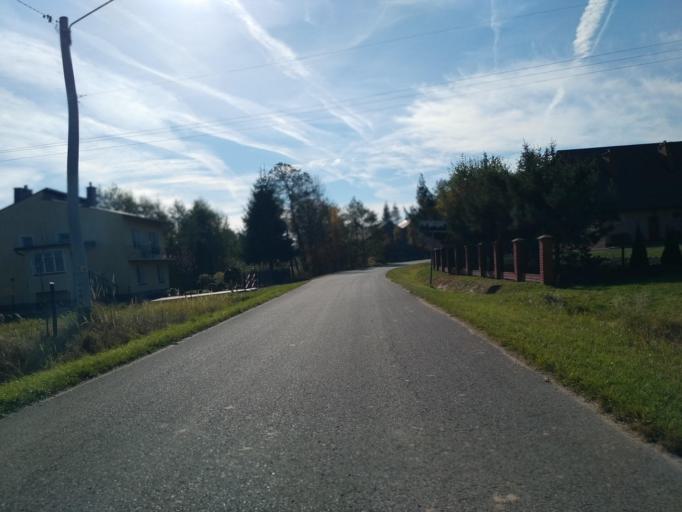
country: PL
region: Subcarpathian Voivodeship
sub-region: Powiat rzeszowski
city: Trzciana
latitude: 50.0847
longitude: 21.8136
